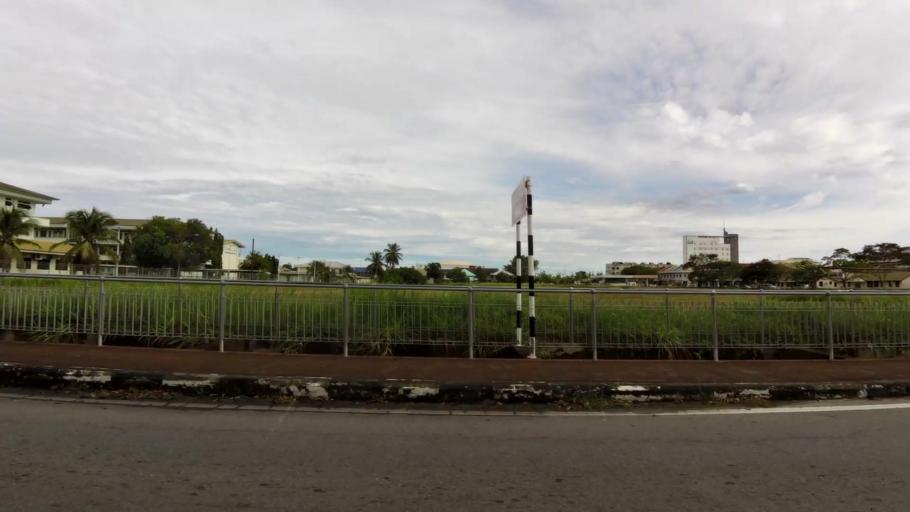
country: BN
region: Belait
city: Seria
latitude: 4.6114
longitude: 114.3290
